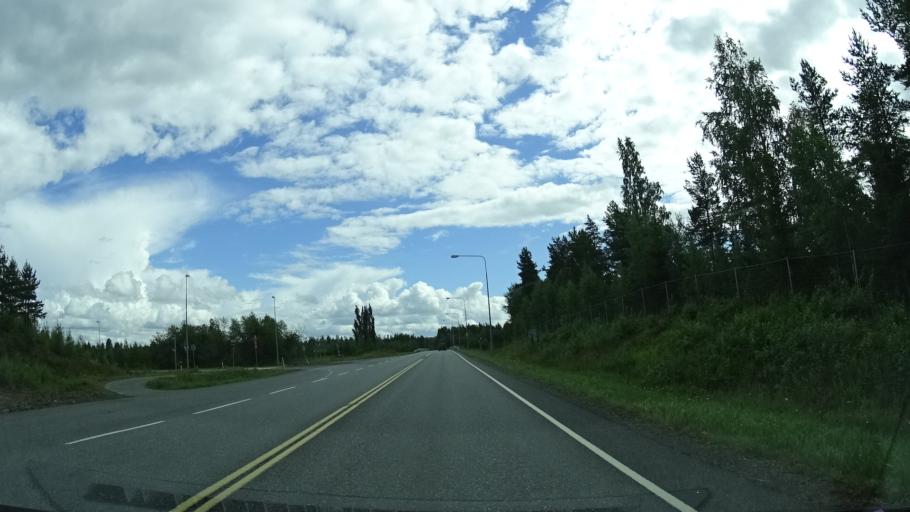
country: FI
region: Haeme
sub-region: Haemeenlinna
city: Kalvola
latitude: 61.1420
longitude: 24.0647
